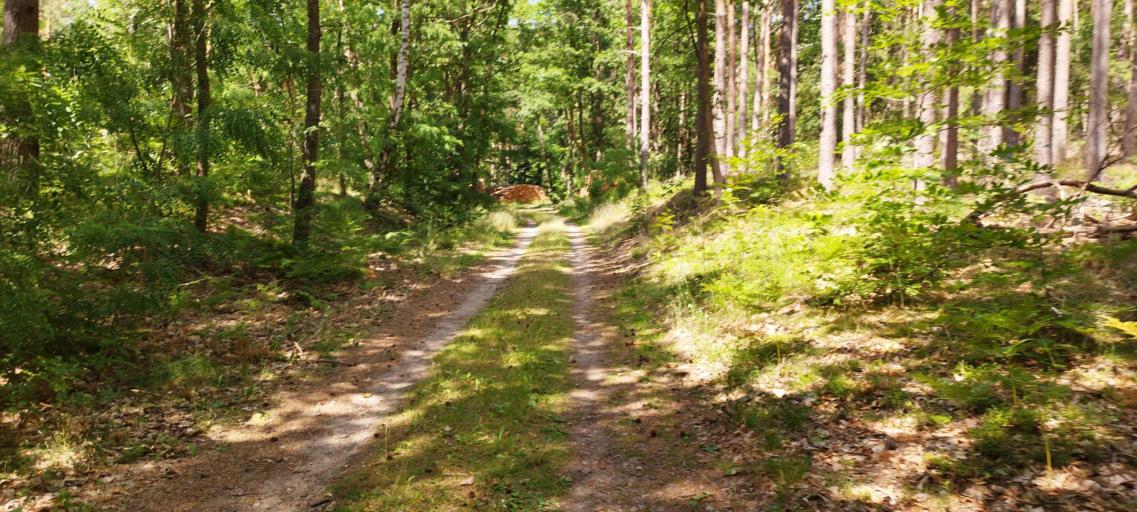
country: DE
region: Brandenburg
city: Rauen
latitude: 52.3109
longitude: 14.0280
